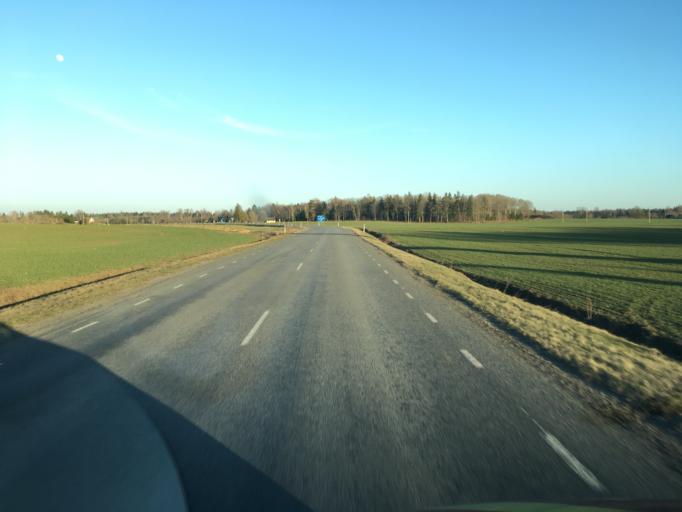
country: EE
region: Raplamaa
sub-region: Kehtna vald
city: Kehtna
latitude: 59.0583
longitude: 24.9422
